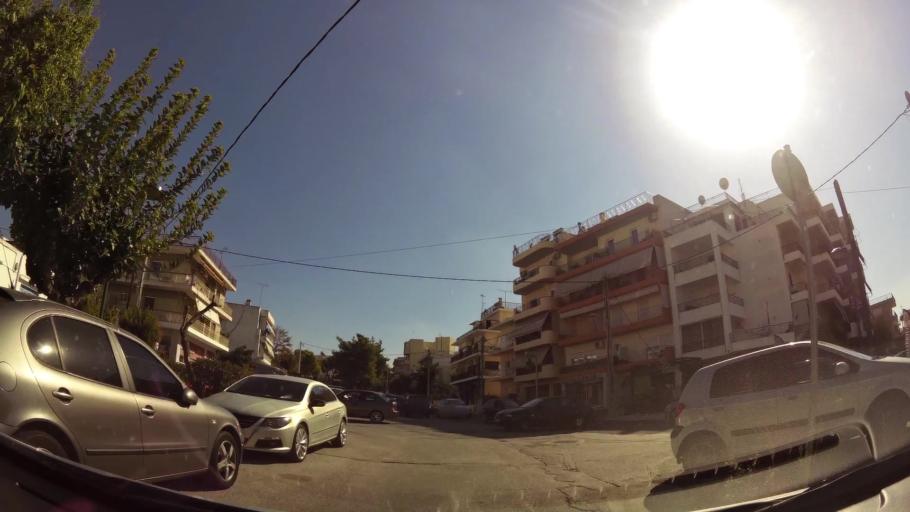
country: GR
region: Attica
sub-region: Nomarchia Athinas
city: Metamorfosi
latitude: 38.0656
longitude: 23.7637
